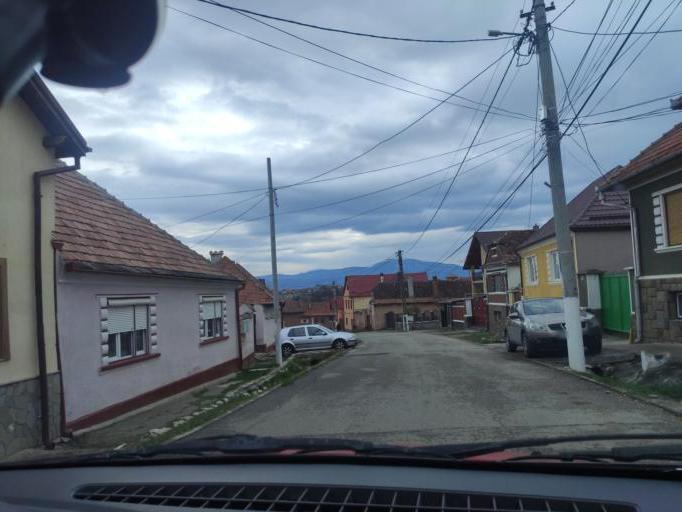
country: RO
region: Brasov
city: Codlea
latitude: 45.6974
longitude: 25.4352
